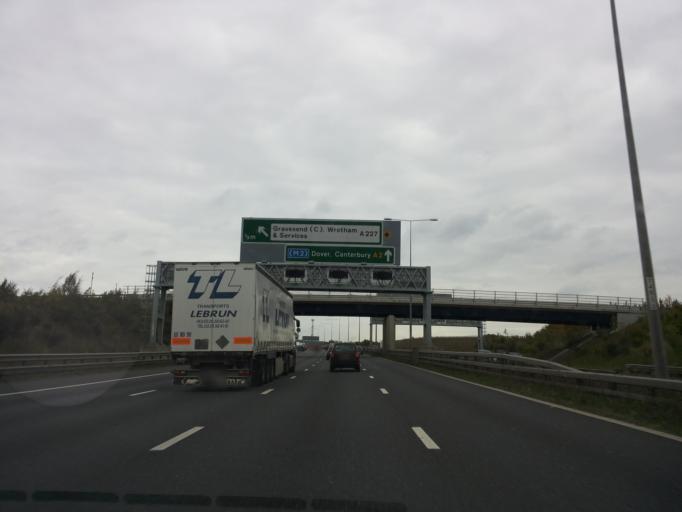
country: GB
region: England
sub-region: Kent
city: Gravesend
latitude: 51.4210
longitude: 0.3422
